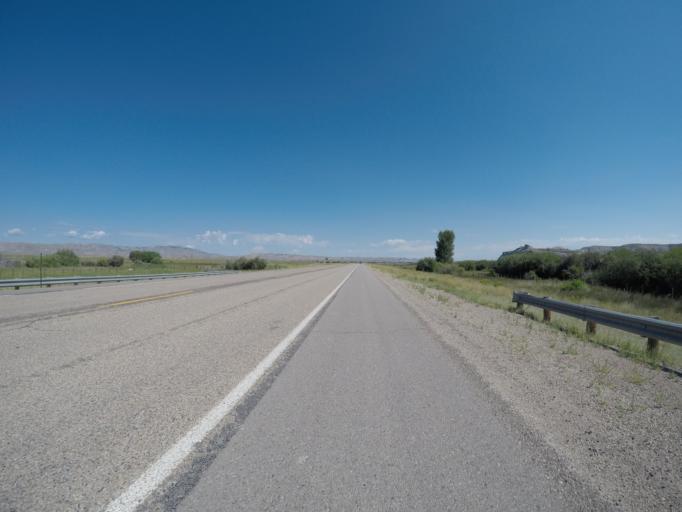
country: US
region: Wyoming
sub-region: Sublette County
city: Marbleton
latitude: 42.2281
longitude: -110.1922
